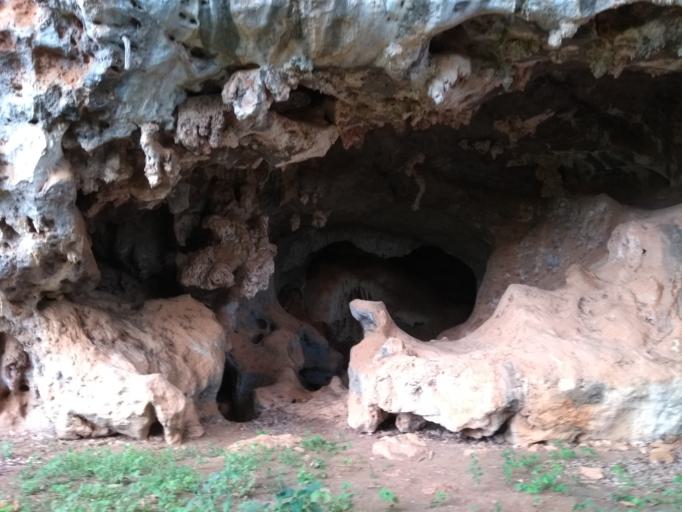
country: BR
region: Goias
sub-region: Formosa
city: Formosa
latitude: -15.4931
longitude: -47.3026
